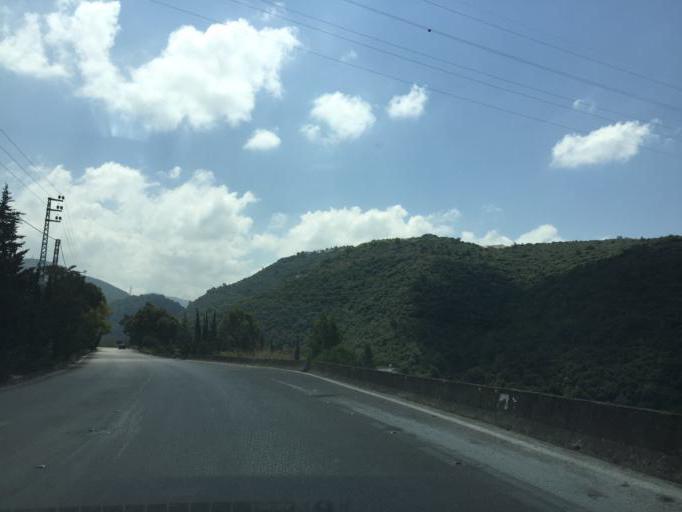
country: LB
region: Mont-Liban
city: Beit ed Dine
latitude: 33.7072
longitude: 35.4589
